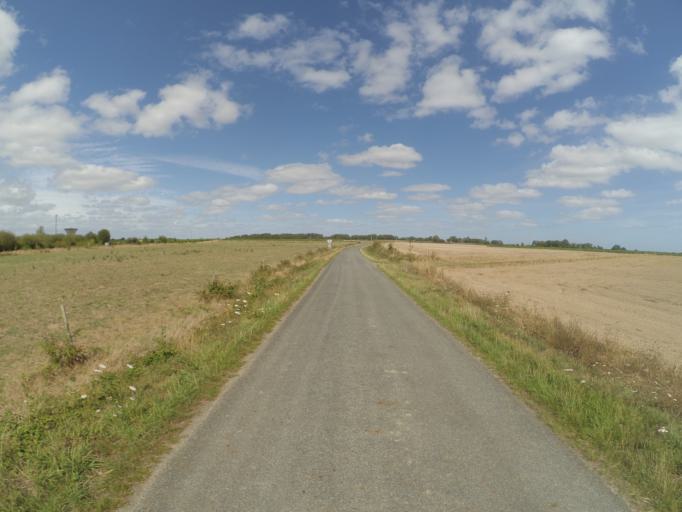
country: FR
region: Pays de la Loire
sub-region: Departement de la Loire-Atlantique
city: La Planche
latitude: 47.0367
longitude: -1.4161
